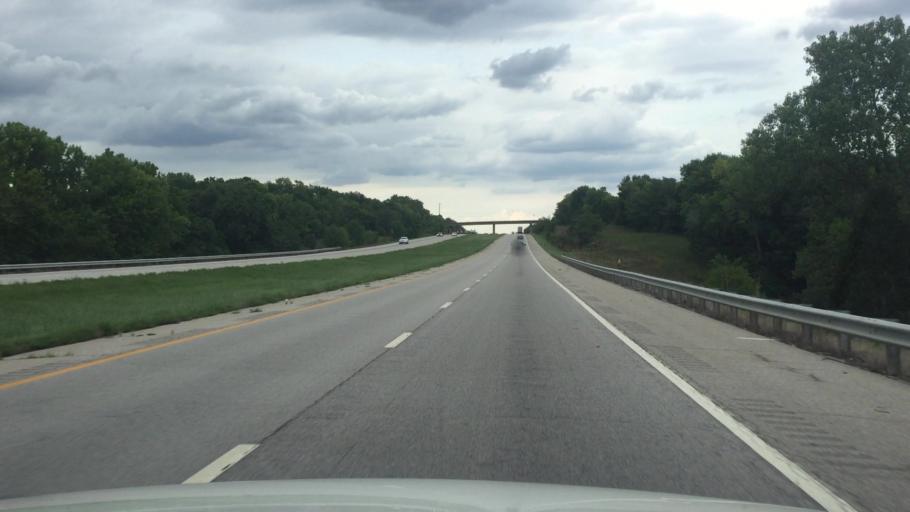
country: US
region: Missouri
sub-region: Cass County
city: Belton
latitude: 38.7917
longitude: -94.6765
